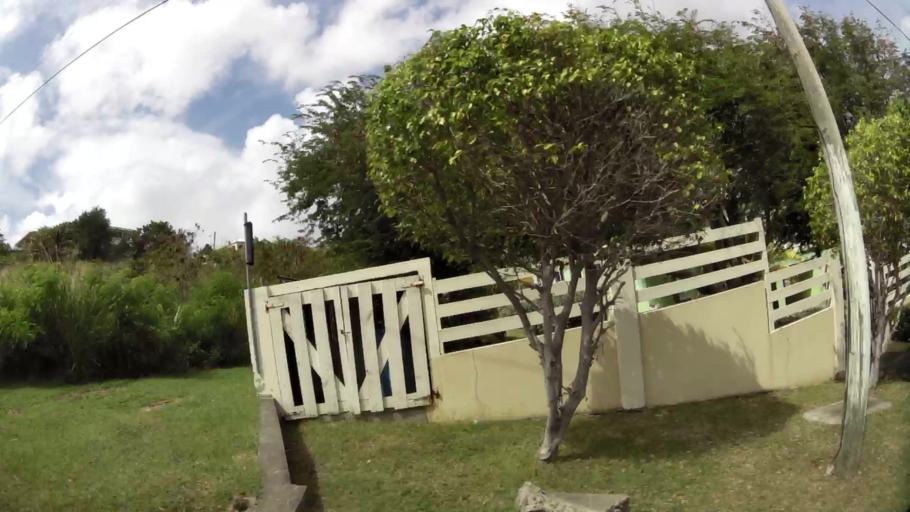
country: KN
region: Saint George Basseterre
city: Basseterre
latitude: 17.2847
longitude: -62.6932
